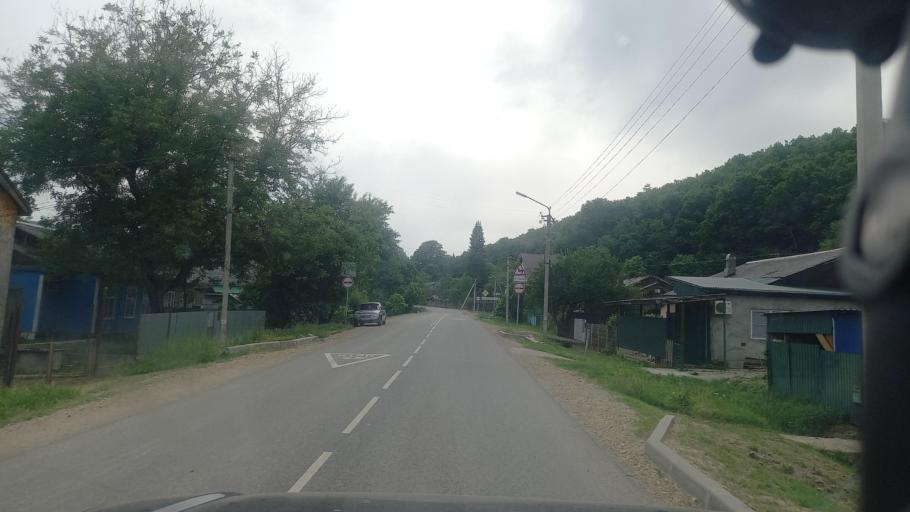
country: RU
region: Krasnodarskiy
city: Goryachiy Klyuch
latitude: 44.6047
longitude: 39.0106
